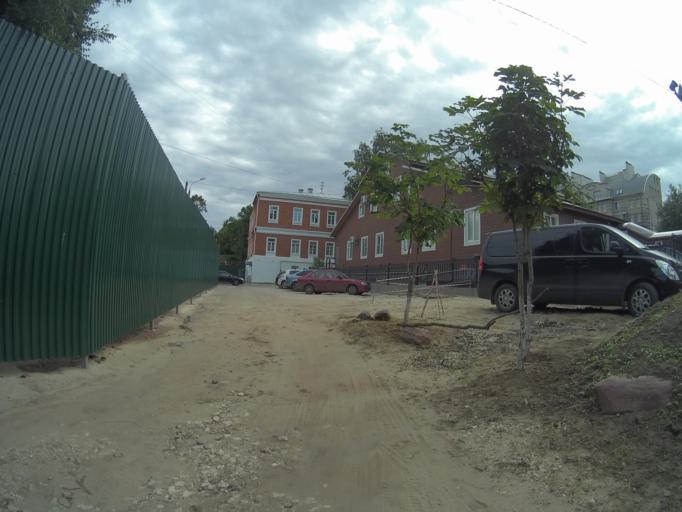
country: RU
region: Vladimir
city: Vladimir
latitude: 56.1247
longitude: 40.3873
